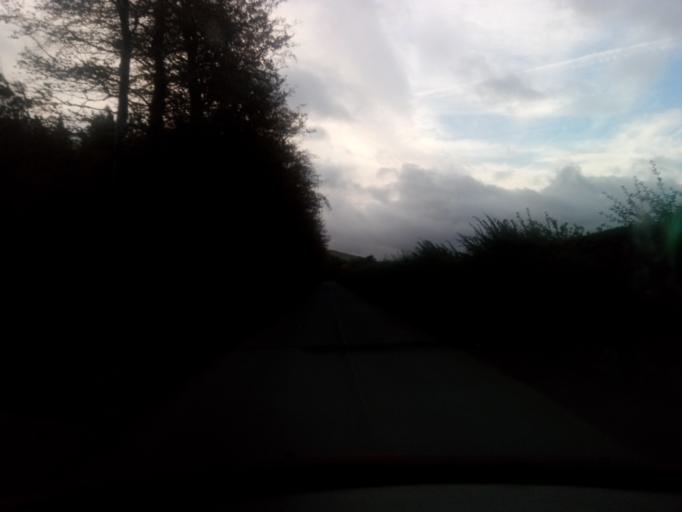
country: GB
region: Scotland
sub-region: The Scottish Borders
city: Jedburgh
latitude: 55.3876
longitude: -2.6433
